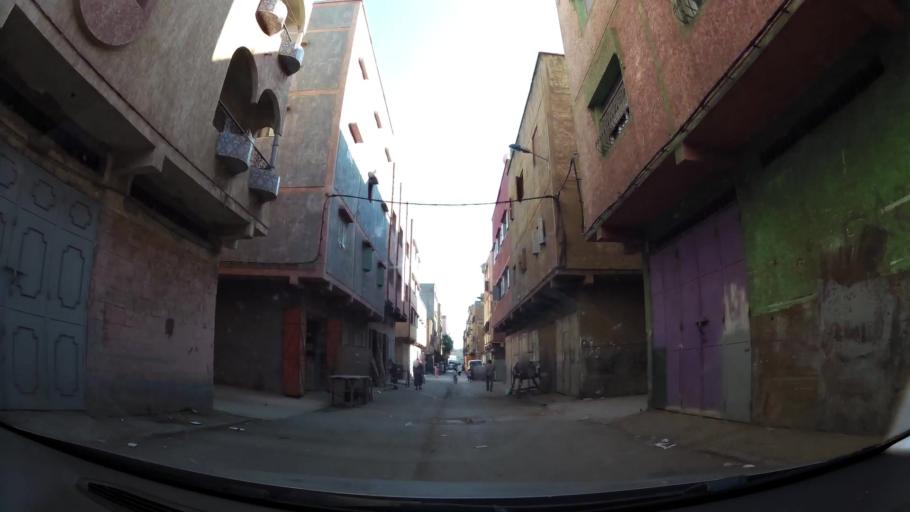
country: MA
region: Rabat-Sale-Zemmour-Zaer
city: Sale
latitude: 34.0598
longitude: -6.7886
